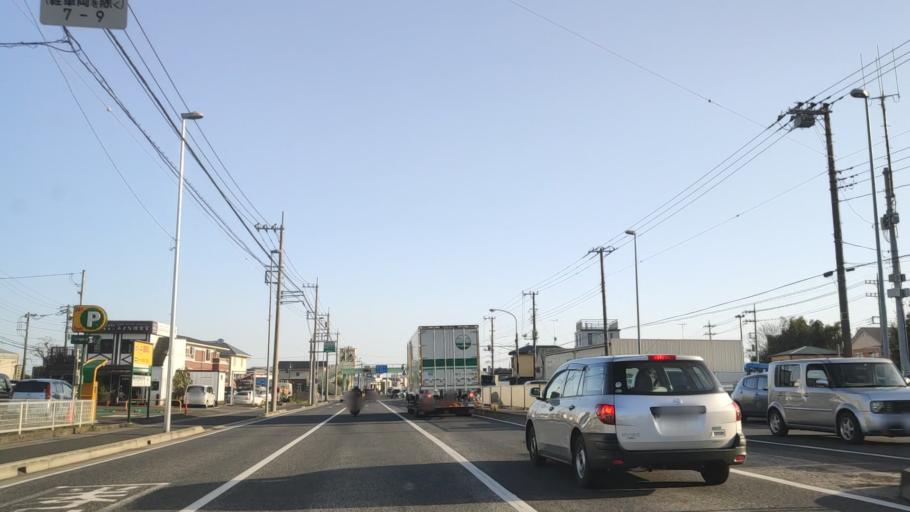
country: JP
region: Kanagawa
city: Zama
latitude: 35.4770
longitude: 139.3667
